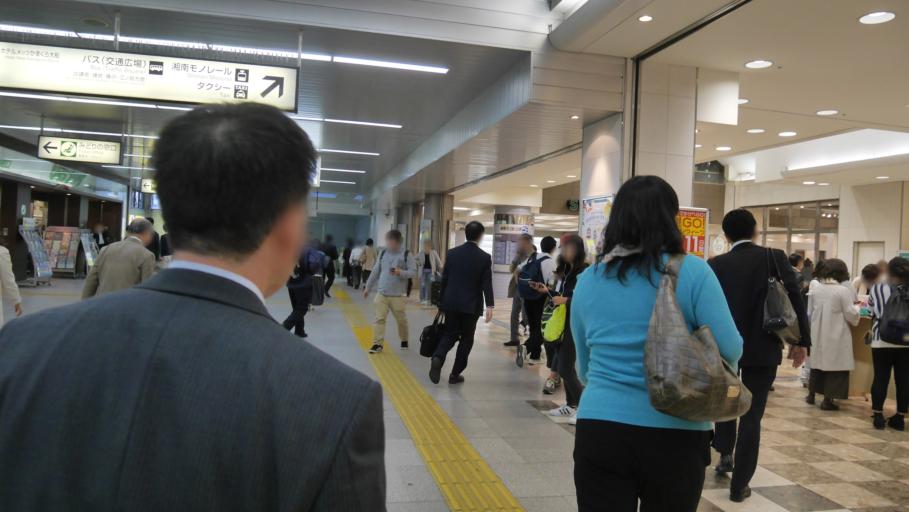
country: JP
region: Kanagawa
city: Kamakura
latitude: 35.3534
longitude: 139.5311
